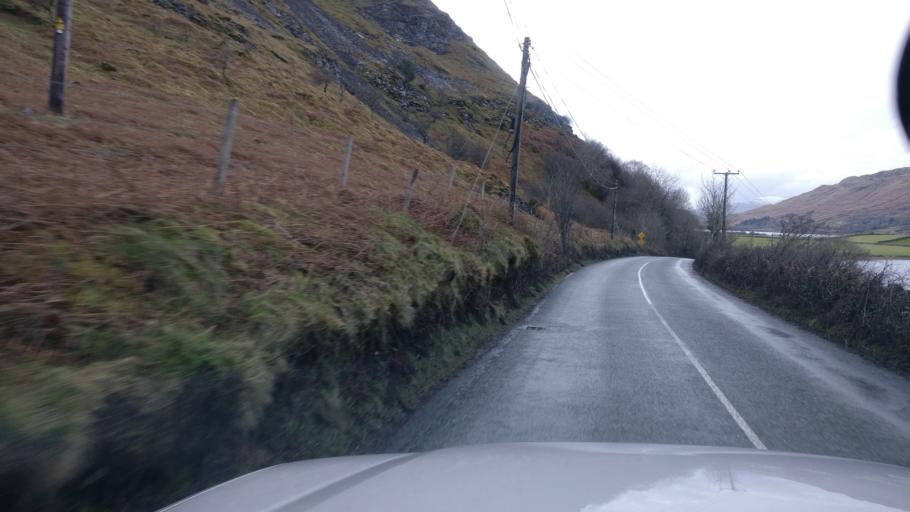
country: IE
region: Connaught
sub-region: County Galway
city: Oughterard
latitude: 53.5604
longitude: -9.4301
